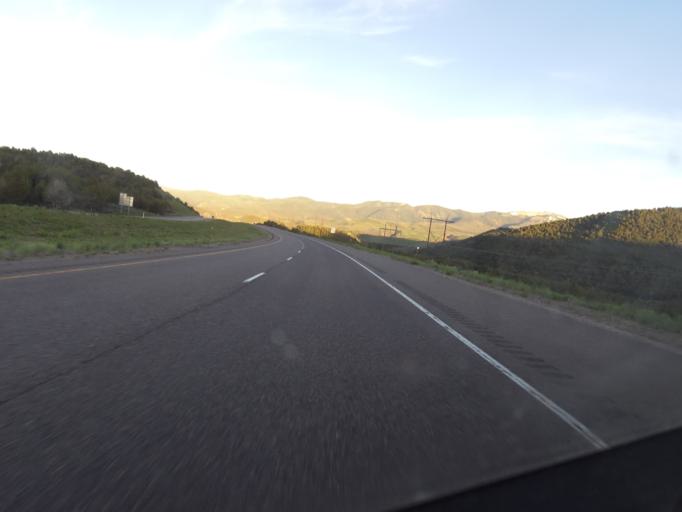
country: US
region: Utah
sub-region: Beaver County
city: Beaver
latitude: 38.5801
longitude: -112.4819
